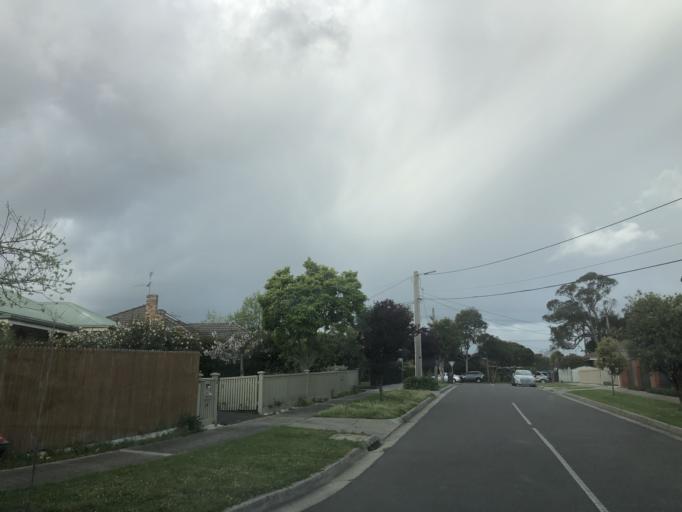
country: AU
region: Victoria
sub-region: Monash
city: Notting Hill
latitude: -37.8855
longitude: 145.1261
